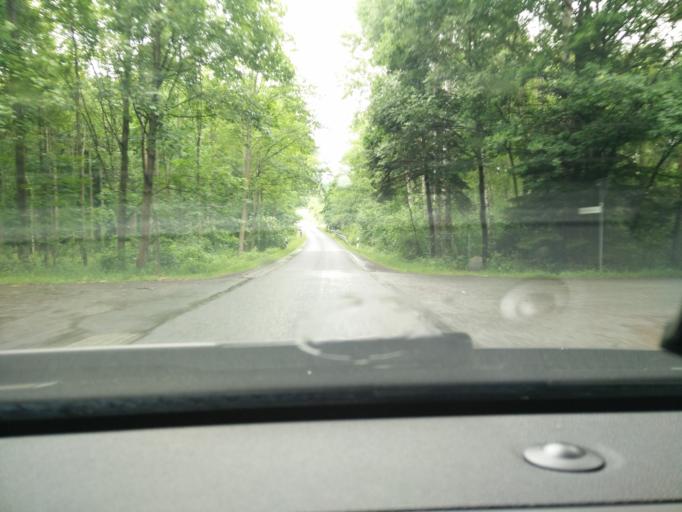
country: DE
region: Saxony
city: Bad Lausick
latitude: 51.1226
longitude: 12.6859
